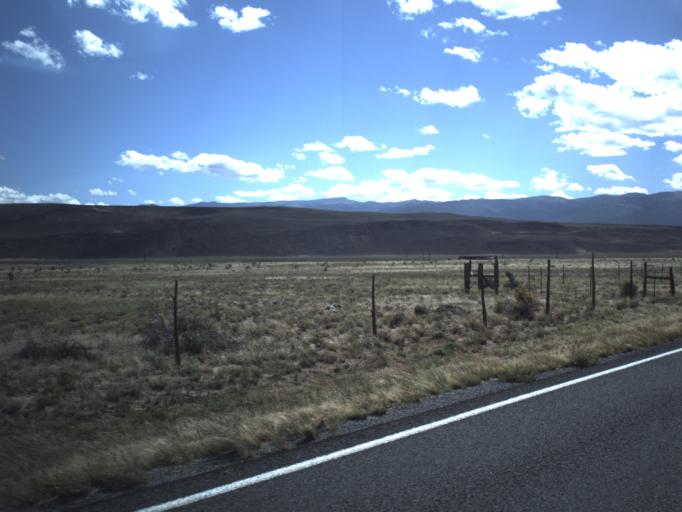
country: US
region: Utah
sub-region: Iron County
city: Enoch
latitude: 37.8942
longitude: -113.0316
